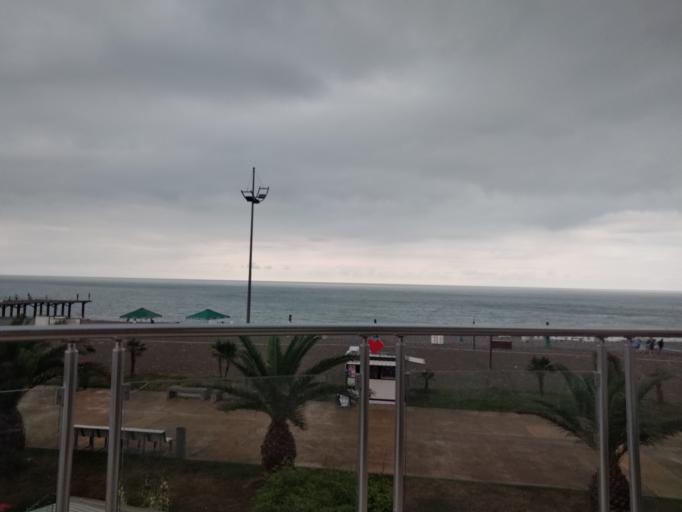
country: GE
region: Ajaria
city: Batumi
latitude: 41.6397
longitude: 41.6107
